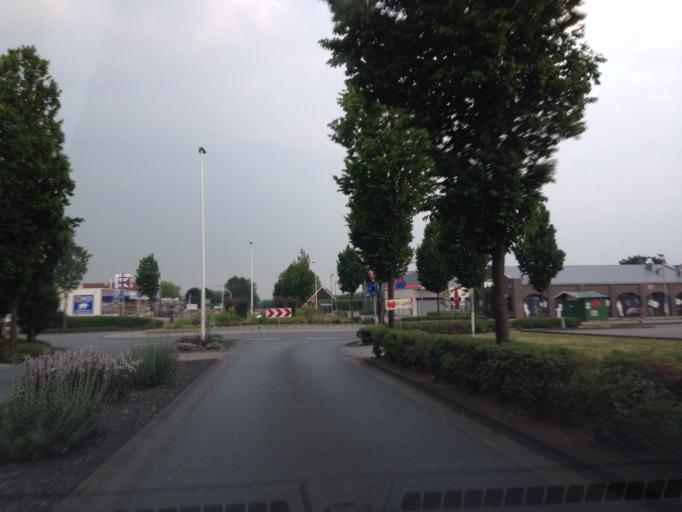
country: DE
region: North Rhine-Westphalia
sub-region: Regierungsbezirk Munster
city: Nottuln
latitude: 51.9266
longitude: 7.3640
